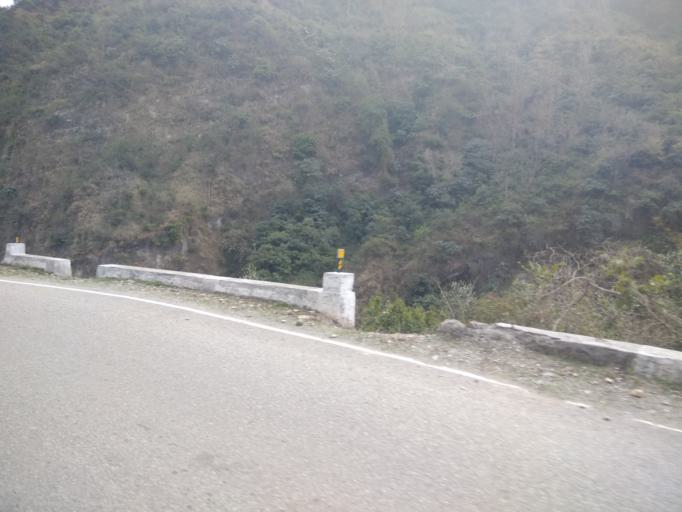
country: IN
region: Himachal Pradesh
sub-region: Kangra
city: Kotla
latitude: 32.2252
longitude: 76.0610
